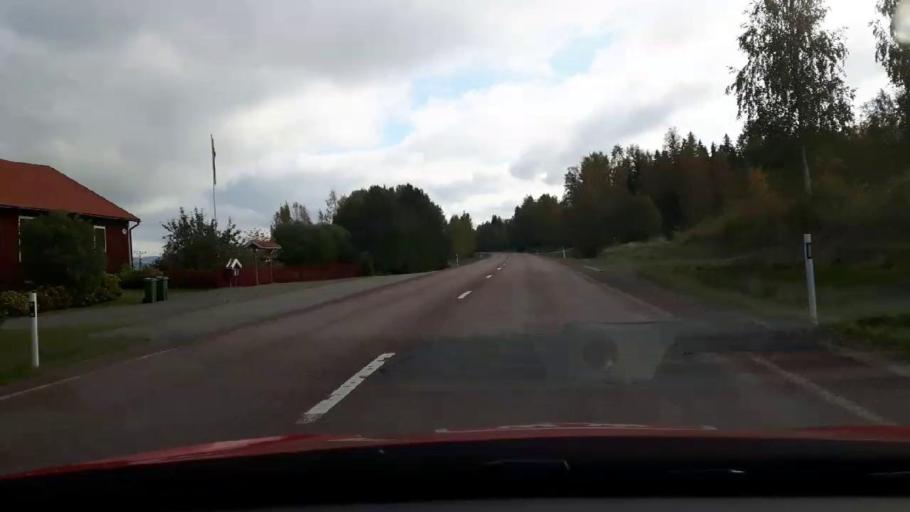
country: SE
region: Gaevleborg
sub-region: Ljusdals Kommun
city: Jaervsoe
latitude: 61.6467
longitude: 16.2024
